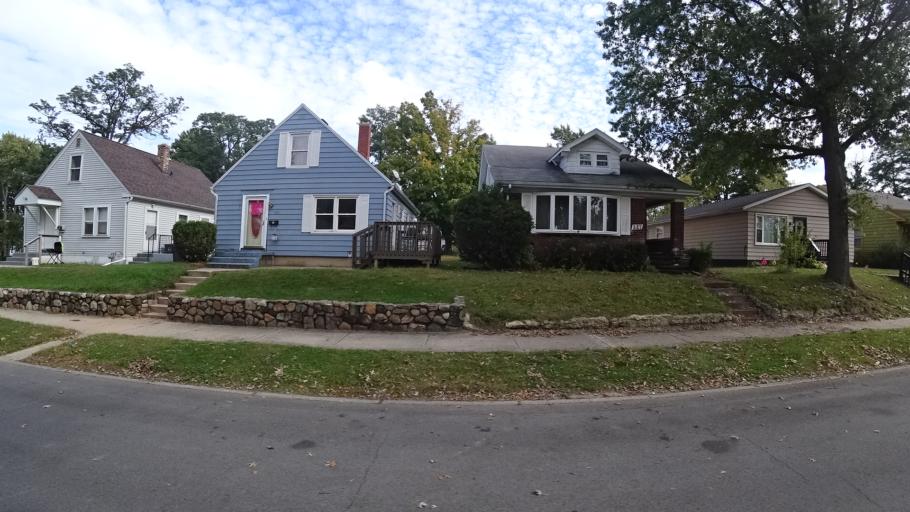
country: US
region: Indiana
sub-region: LaPorte County
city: Trail Creek
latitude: 41.7116
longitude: -86.8718
